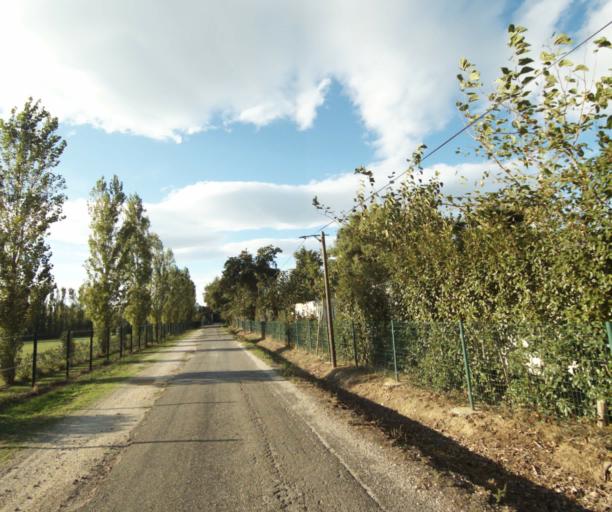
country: FR
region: Languedoc-Roussillon
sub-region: Departement des Pyrenees-Orientales
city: Argelers
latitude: 42.5678
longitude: 3.0129
